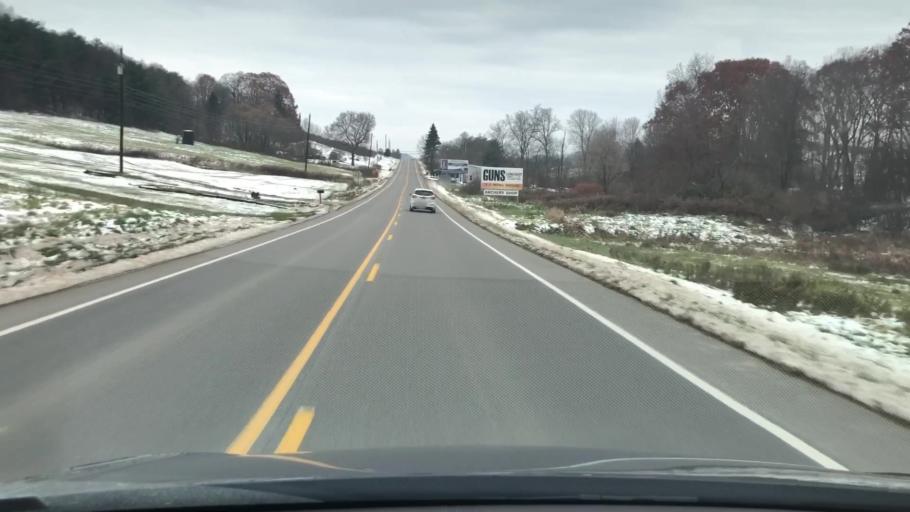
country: US
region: Pennsylvania
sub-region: Jefferson County
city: Brookville
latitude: 41.1045
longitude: -79.2192
